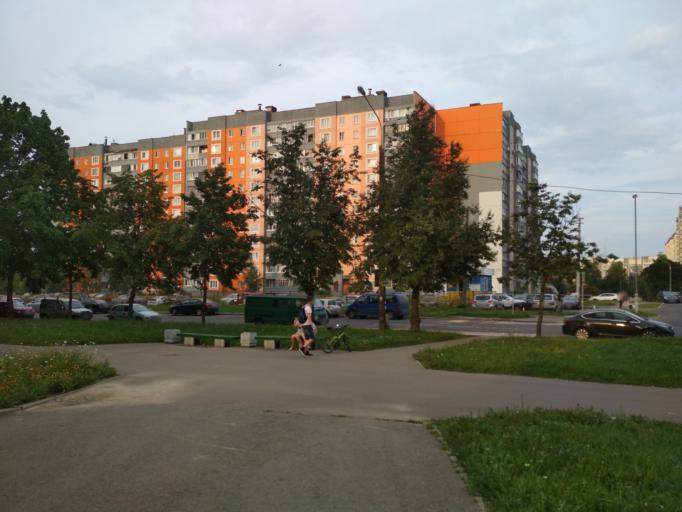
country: BY
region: Minsk
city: Minsk
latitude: 53.8793
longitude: 27.5494
